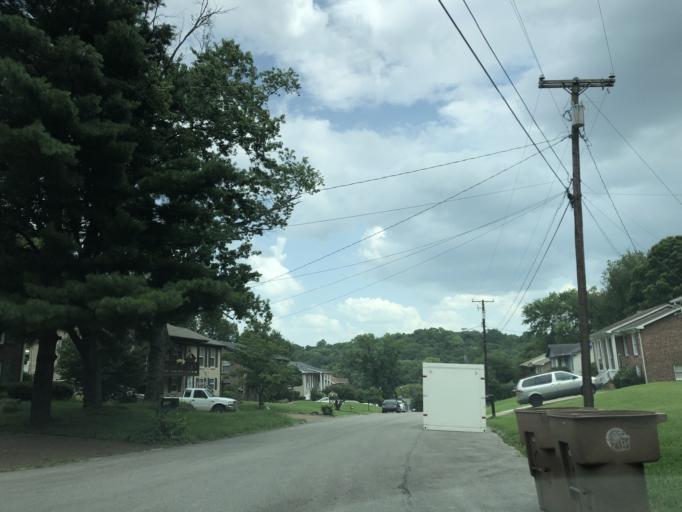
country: US
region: Tennessee
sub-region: Williamson County
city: Brentwood Estates
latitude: 36.0547
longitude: -86.6855
